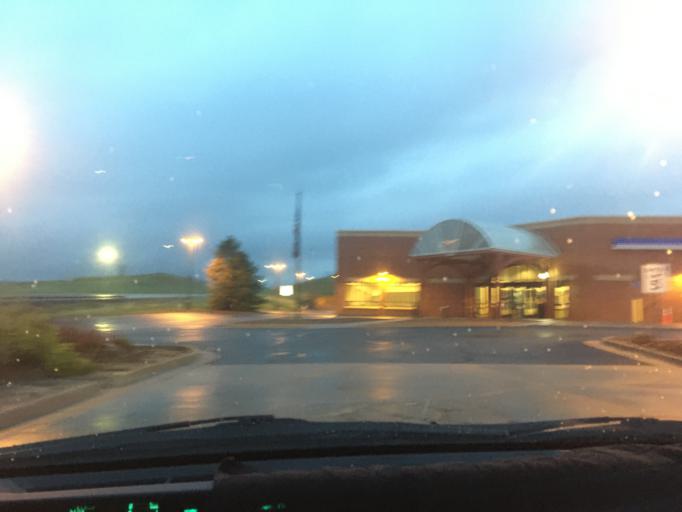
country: US
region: Colorado
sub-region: Broomfield County
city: Broomfield
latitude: 39.9033
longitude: -105.0970
